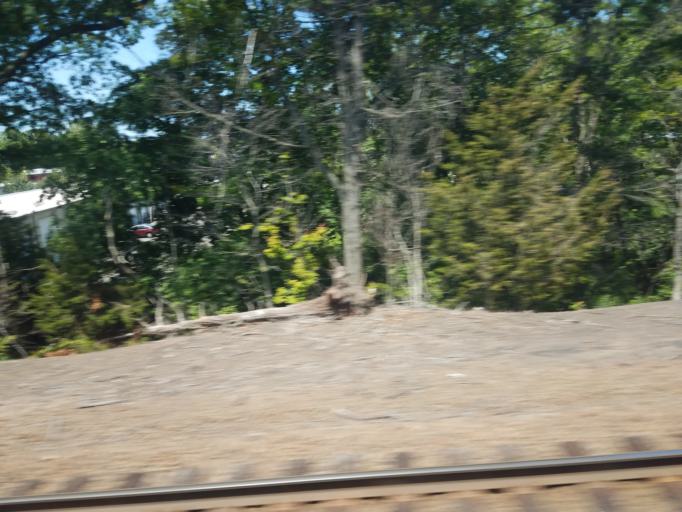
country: US
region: Connecticut
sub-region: New Haven County
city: Wallingford
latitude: 41.4752
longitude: -72.8151
